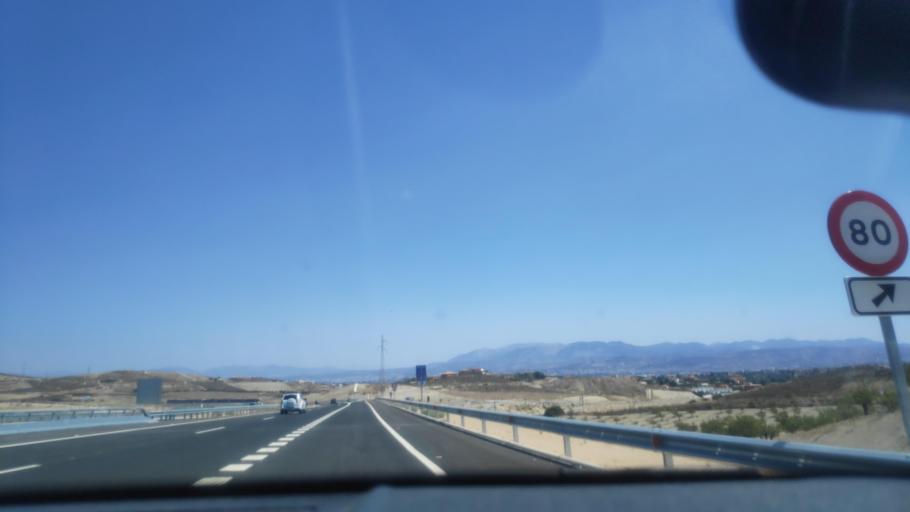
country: ES
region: Andalusia
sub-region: Provincia de Granada
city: Alhendin
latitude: 37.0990
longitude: -3.6734
